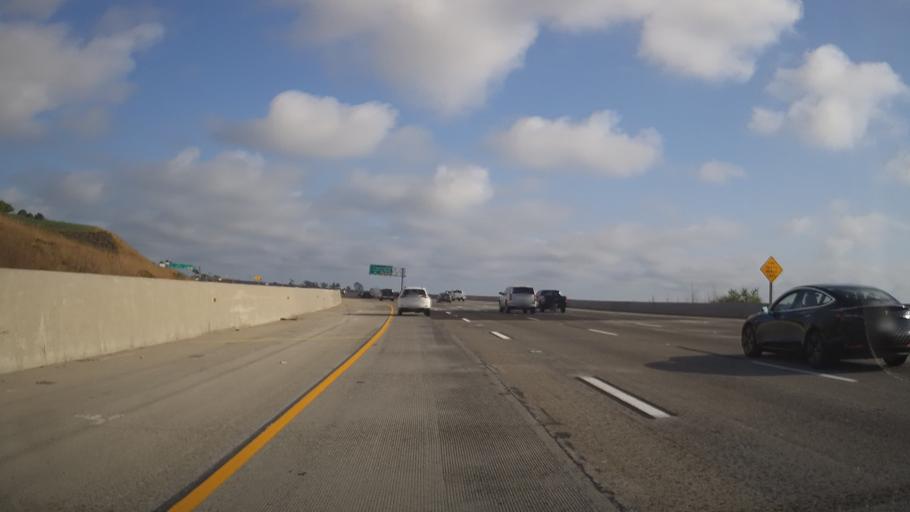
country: US
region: California
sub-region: Orange County
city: Dana Point
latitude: 33.4751
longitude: -117.6754
